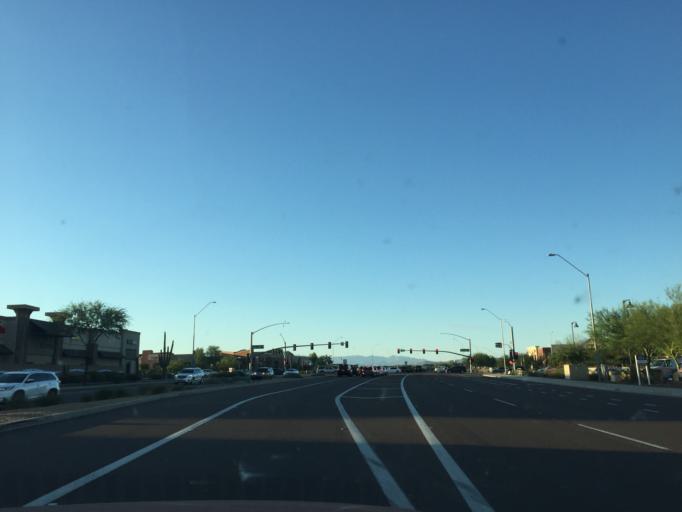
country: US
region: Arizona
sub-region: Maricopa County
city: Sun City West
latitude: 33.7094
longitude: -112.2726
